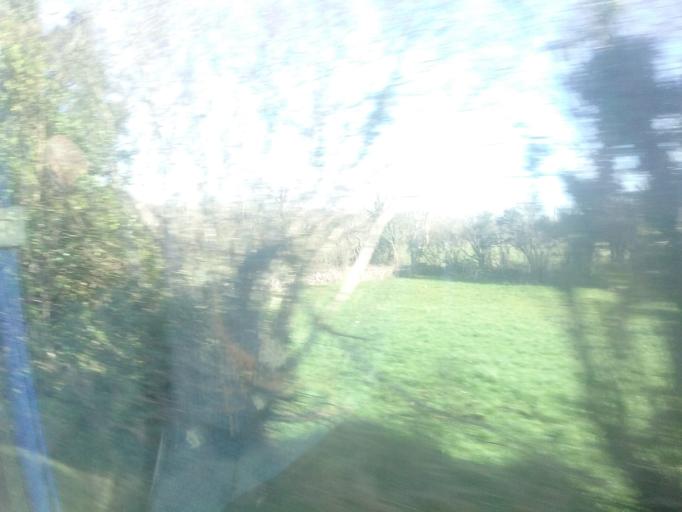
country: IE
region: Munster
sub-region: An Clar
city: Ennis
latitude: 52.9859
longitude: -8.9977
